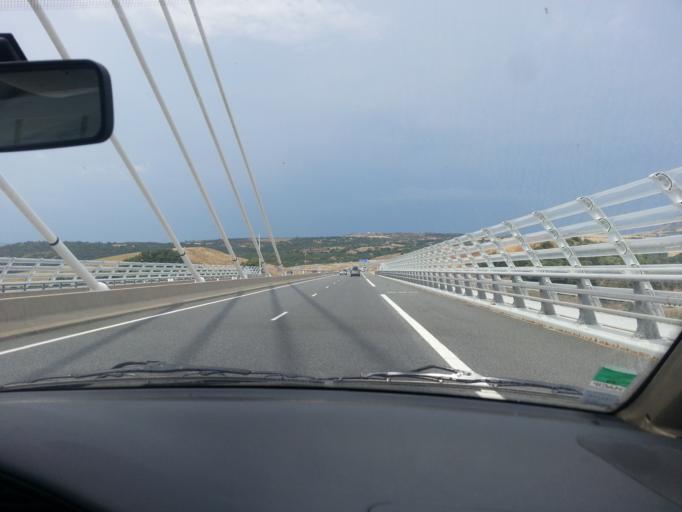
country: FR
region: Midi-Pyrenees
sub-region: Departement de l'Aveyron
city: Creissels
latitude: 44.0898
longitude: 3.0215
